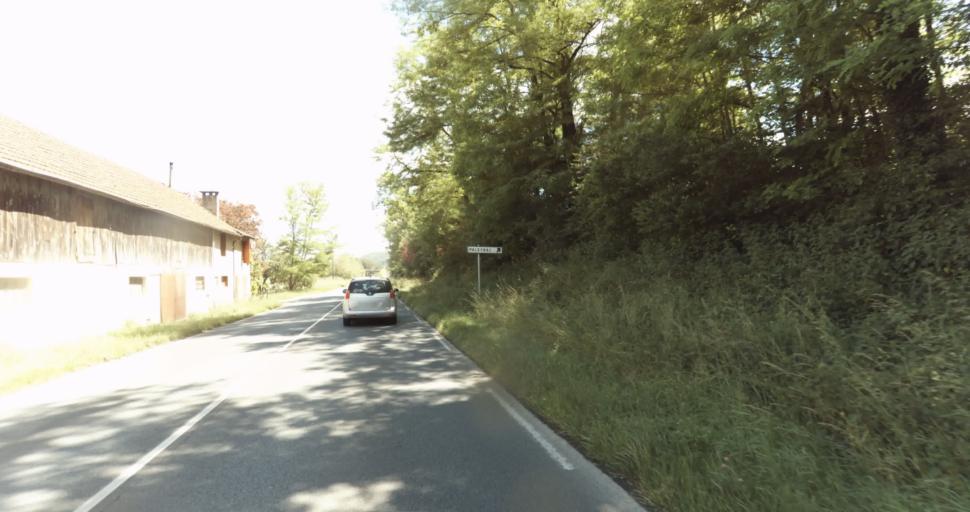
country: FR
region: Aquitaine
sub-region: Departement de la Dordogne
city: Le Bugue
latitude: 44.8370
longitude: 0.9358
